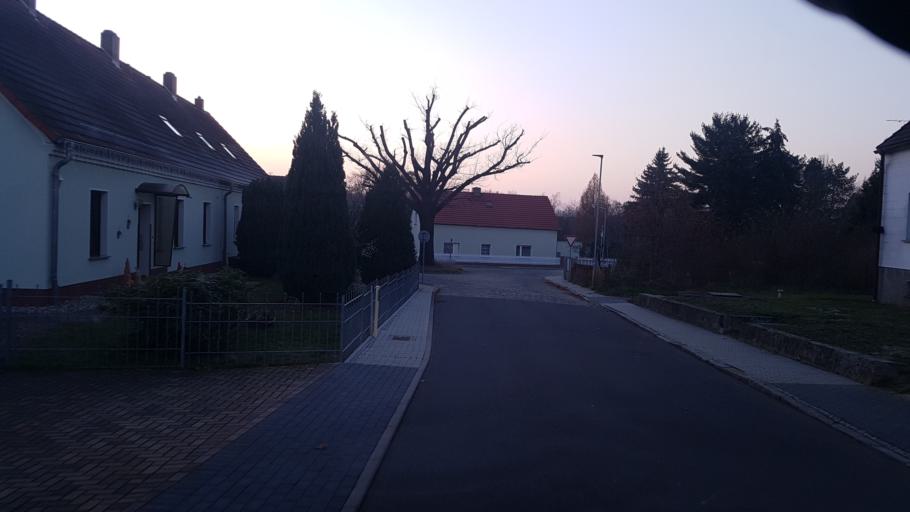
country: DE
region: Brandenburg
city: Lauchhammer
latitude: 51.5136
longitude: 13.7518
